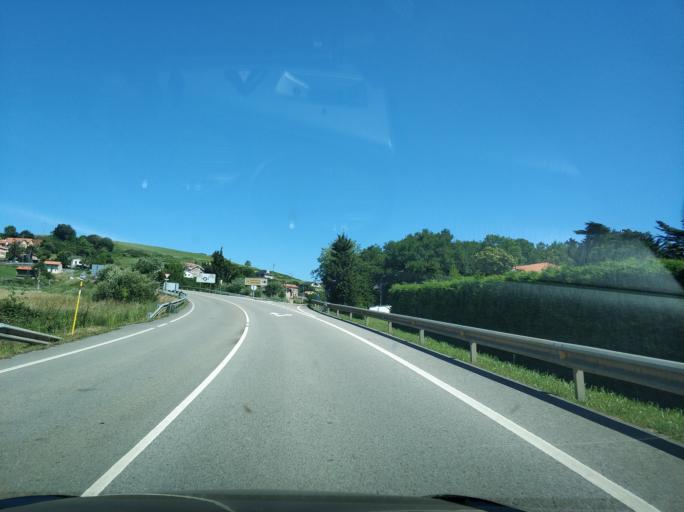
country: ES
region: Cantabria
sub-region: Provincia de Cantabria
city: Camargo
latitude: 43.3889
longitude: -3.8593
